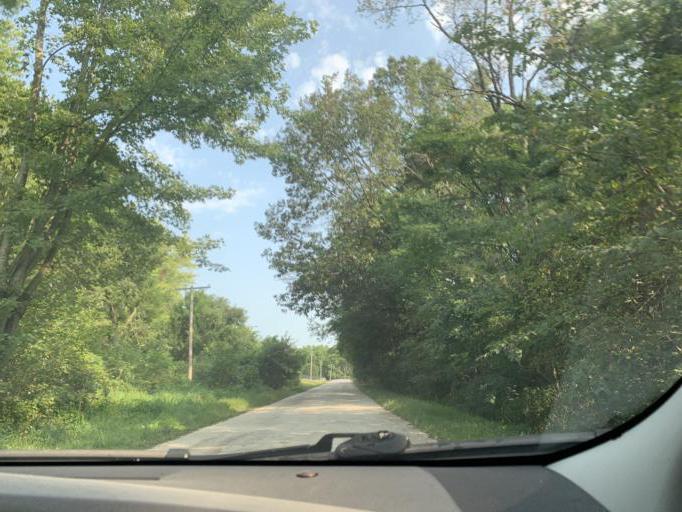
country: US
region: Illinois
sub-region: Whiteside County
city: Morrison
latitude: 41.8742
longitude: -89.9303
